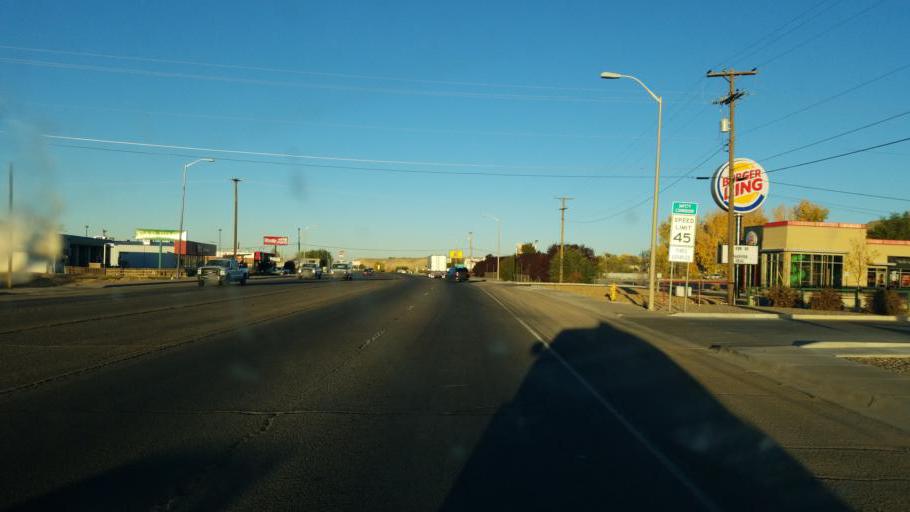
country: US
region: New Mexico
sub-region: San Juan County
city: Farmington
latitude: 36.7321
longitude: -108.2364
